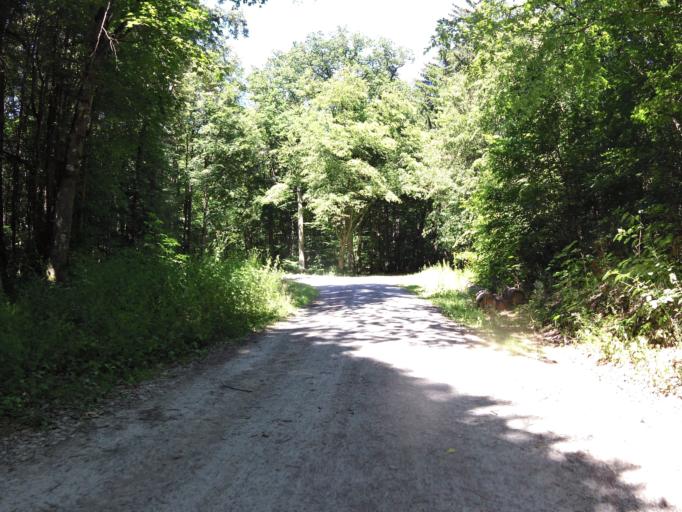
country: DE
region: Bavaria
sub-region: Regierungsbezirk Unterfranken
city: Kleinrinderfeld
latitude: 49.7015
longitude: 9.8677
